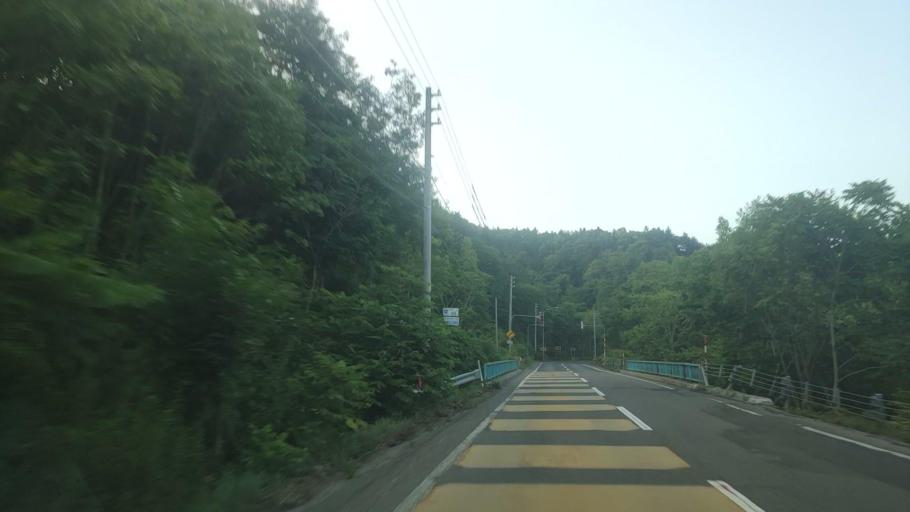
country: JP
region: Hokkaido
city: Bibai
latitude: 43.2509
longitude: 142.0241
